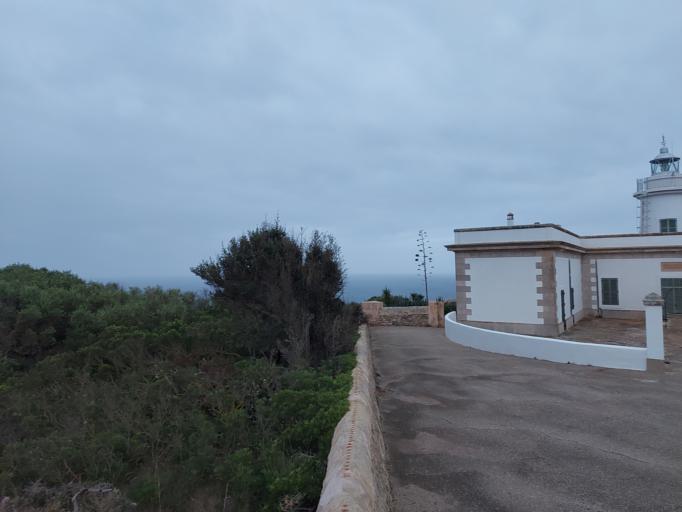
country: ES
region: Balearic Islands
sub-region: Illes Balears
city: s'Arenal
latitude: 39.3637
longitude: 2.7882
